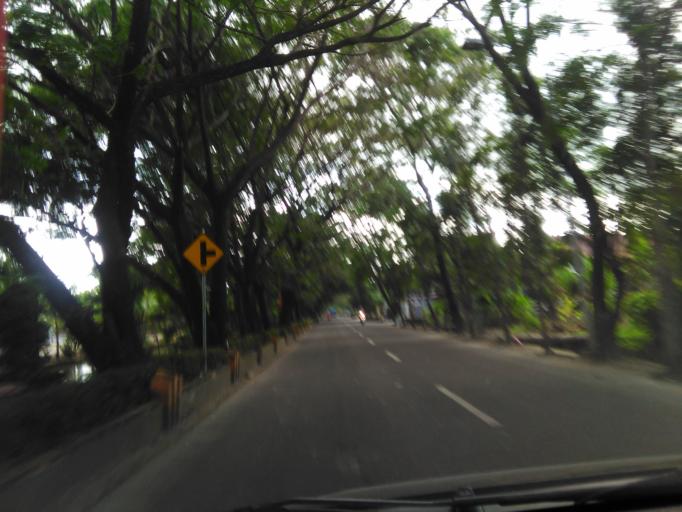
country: ID
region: South Sulawesi
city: Pinrang
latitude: -3.8047
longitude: 119.6464
